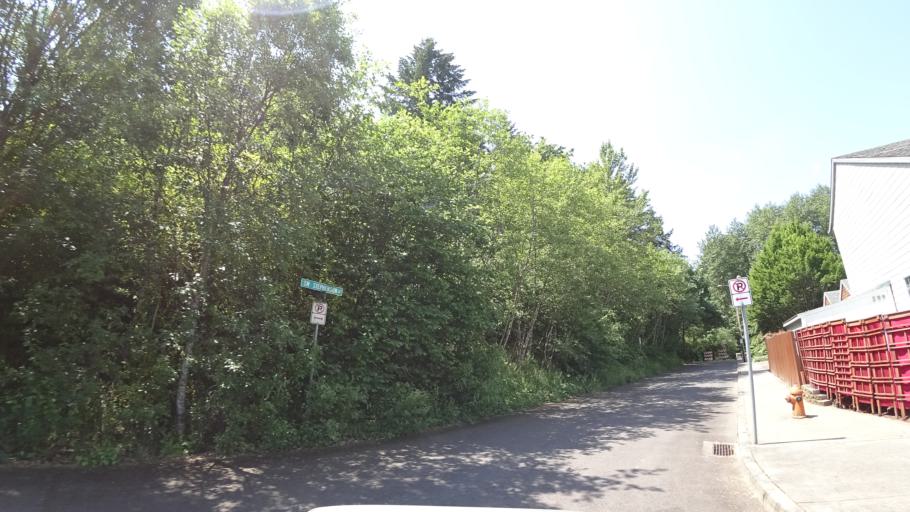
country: US
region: Oregon
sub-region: Washington County
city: Metzger
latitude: 45.4403
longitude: -122.7152
